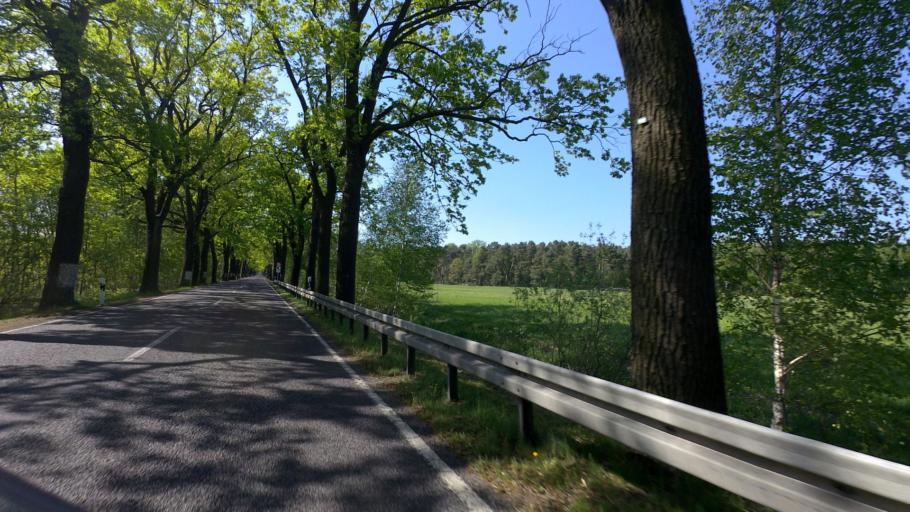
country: DE
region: Brandenburg
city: Munchehofe
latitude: 52.0952
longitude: 13.8433
